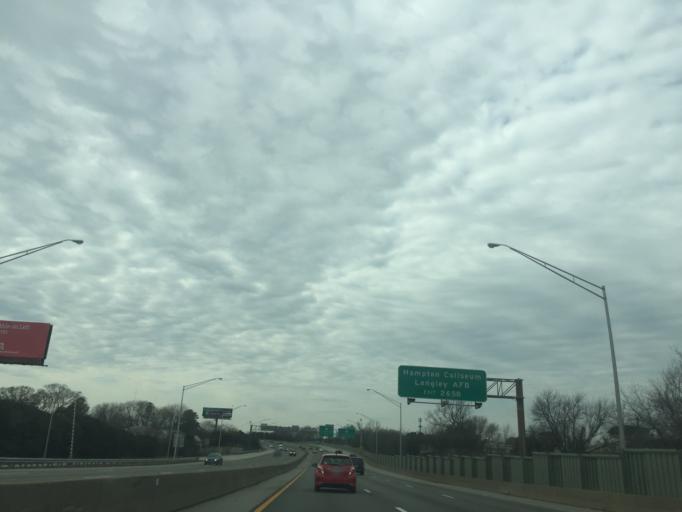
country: US
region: Virginia
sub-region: City of Hampton
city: Hampton
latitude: 37.0349
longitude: -76.3536
